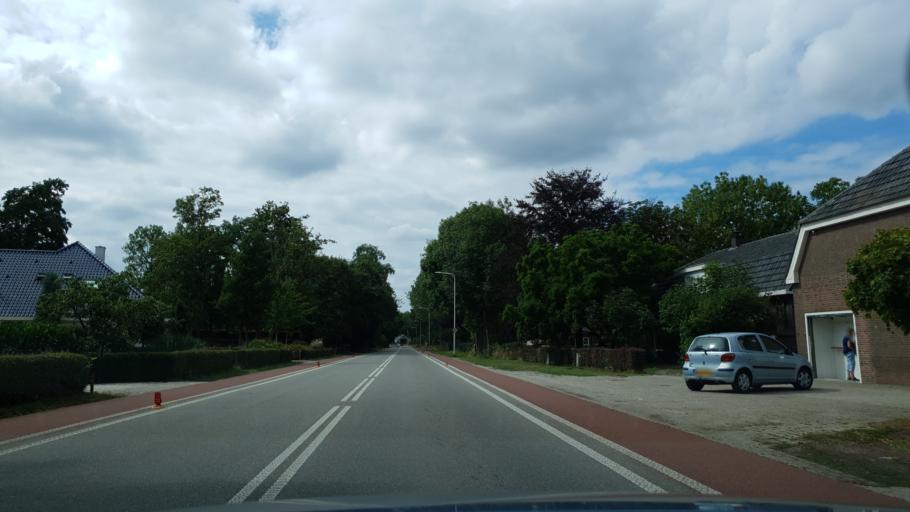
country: NL
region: North Brabant
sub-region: Gemeente Grave
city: Grave
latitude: 51.7668
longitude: 5.7757
